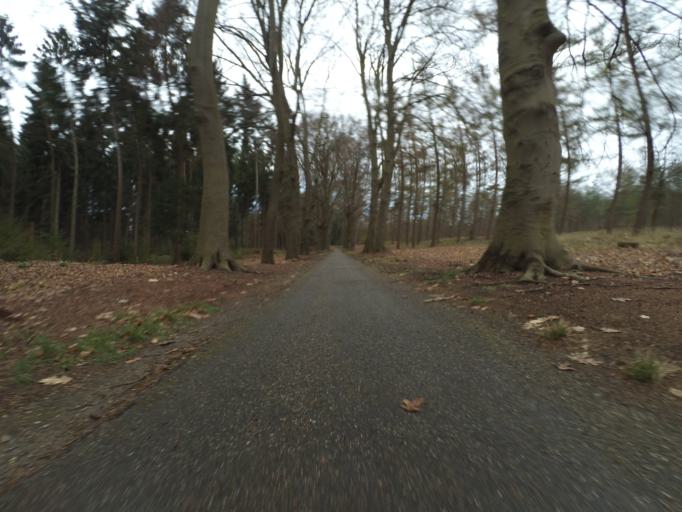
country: NL
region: Gelderland
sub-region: Gemeente Arnhem
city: Gulden Bodem
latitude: 52.0184
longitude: 5.9177
